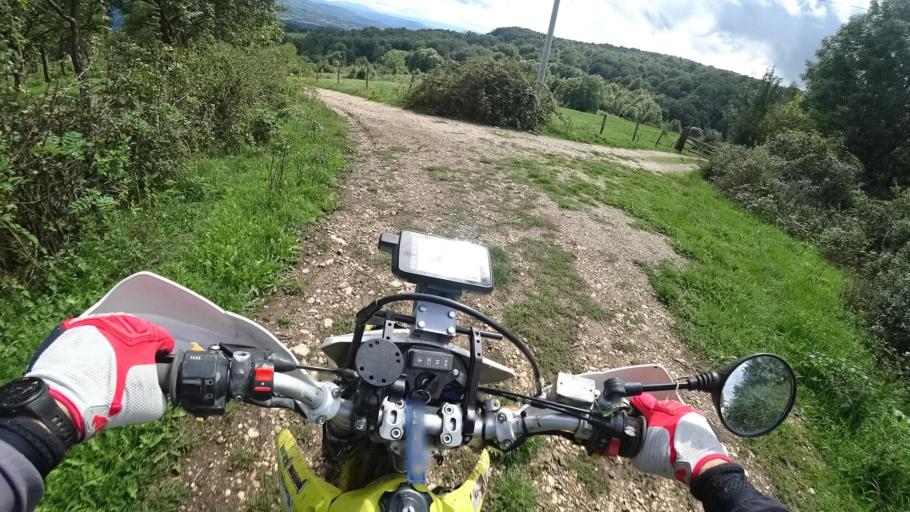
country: BA
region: Republika Srpska
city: Mrkonjic Grad
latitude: 44.5437
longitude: 17.1111
